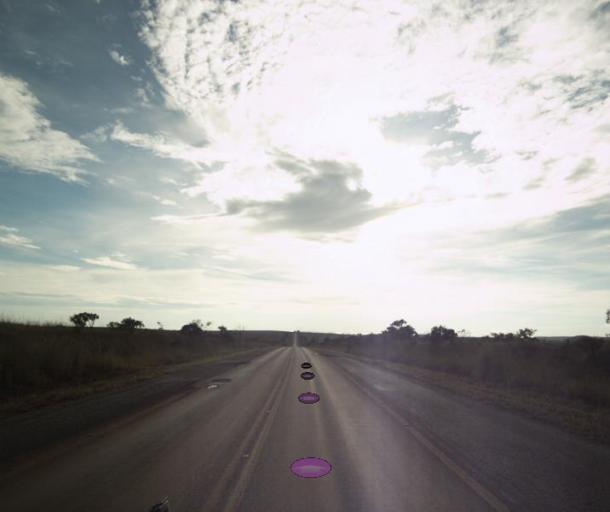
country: BR
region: Goias
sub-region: Pirenopolis
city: Pirenopolis
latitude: -15.7625
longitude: -48.6971
